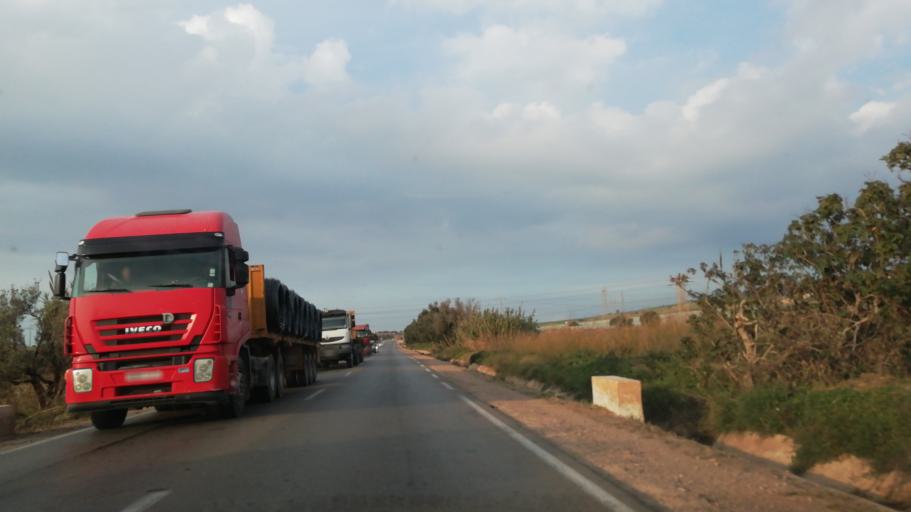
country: DZ
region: Oran
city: Ain el Bya
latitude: 35.7743
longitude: -0.0969
